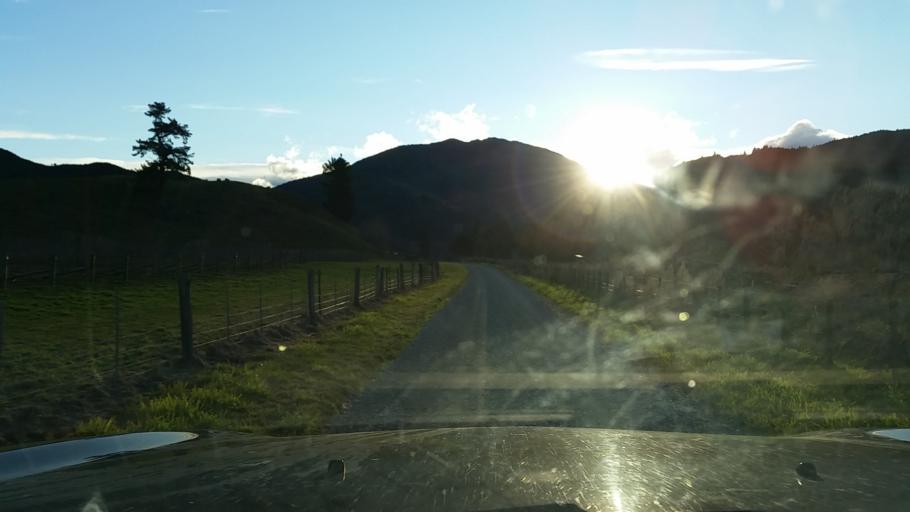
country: NZ
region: Marlborough
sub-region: Marlborough District
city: Blenheim
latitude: -41.5075
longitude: 173.5824
